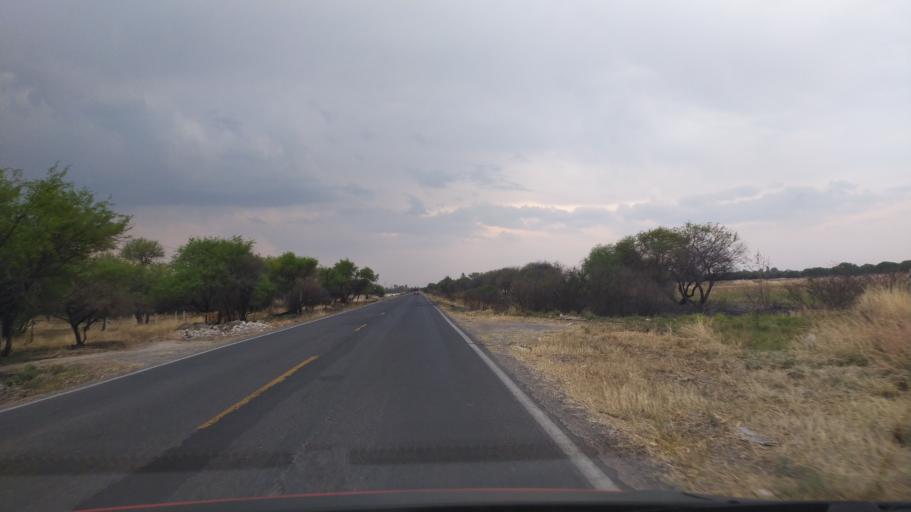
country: MX
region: Guanajuato
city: Ciudad Manuel Doblado
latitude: 20.7739
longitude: -101.9120
